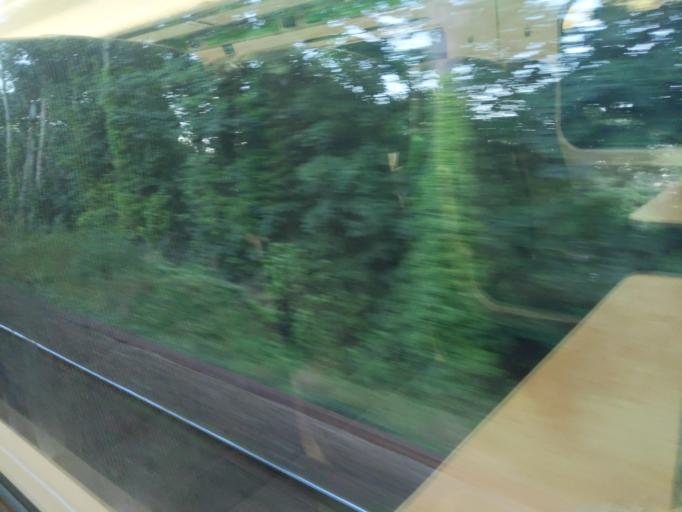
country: GB
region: England
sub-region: Cornwall
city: Truro
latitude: 50.2687
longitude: -5.0512
